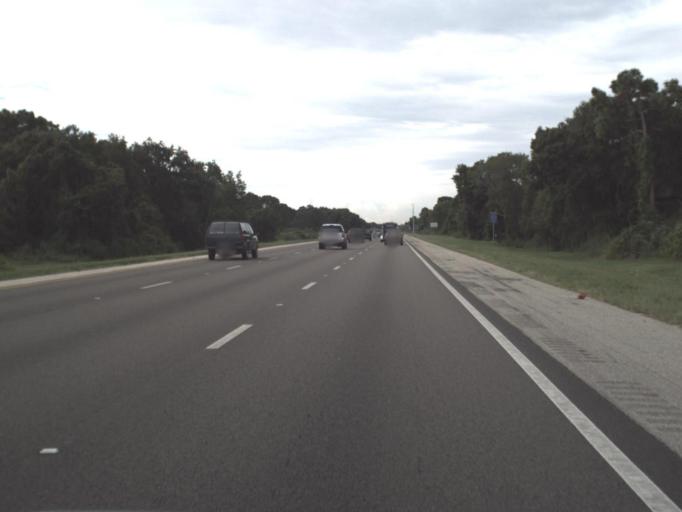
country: US
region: Florida
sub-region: Sarasota County
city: The Meadows
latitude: 27.3777
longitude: -82.4469
